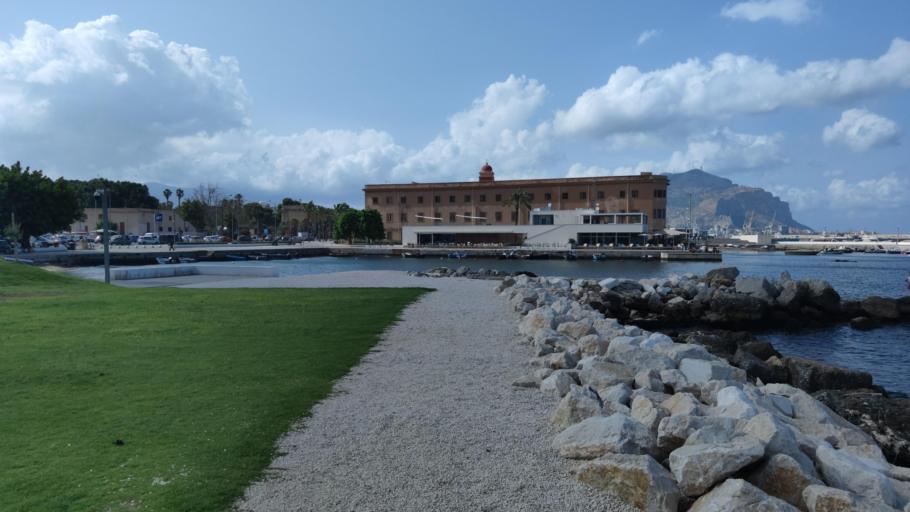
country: IT
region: Sicily
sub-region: Palermo
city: Ciaculli
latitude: 38.1123
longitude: 13.3795
